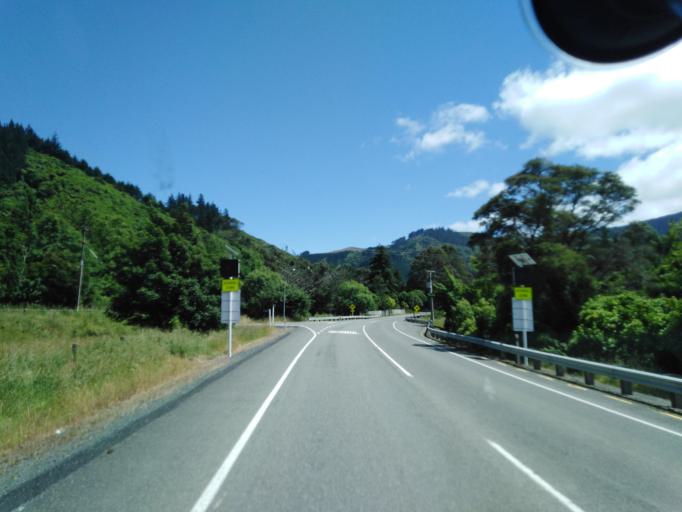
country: NZ
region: Nelson
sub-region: Nelson City
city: Nelson
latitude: -41.2181
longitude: 173.3964
